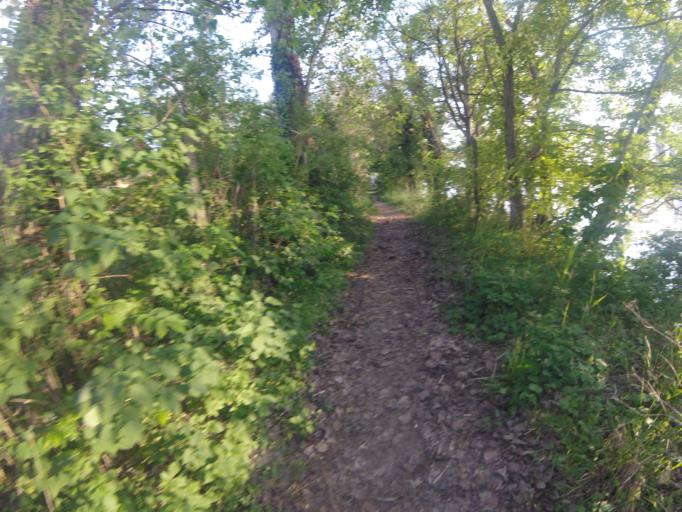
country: HU
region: Pest
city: Rackeve
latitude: 47.1881
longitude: 18.9512
